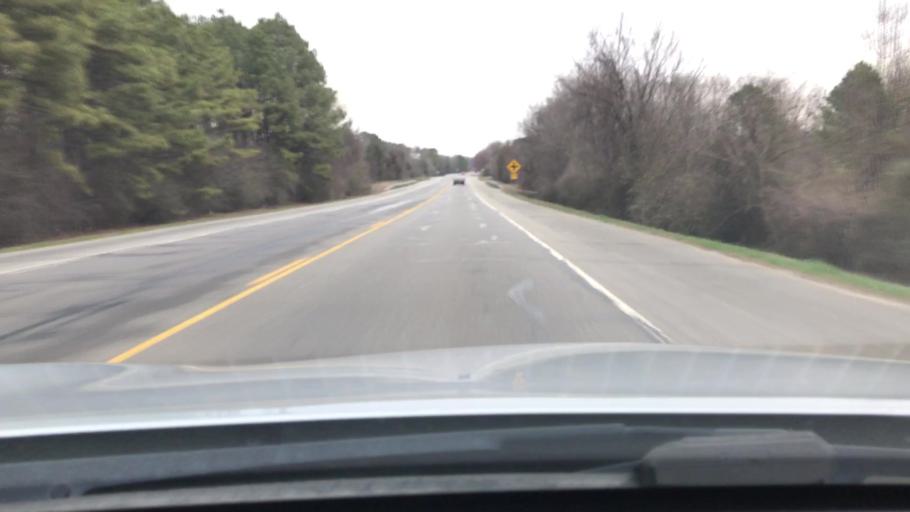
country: US
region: Arkansas
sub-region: Hempstead County
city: Hope
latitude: 33.6879
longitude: -93.5880
